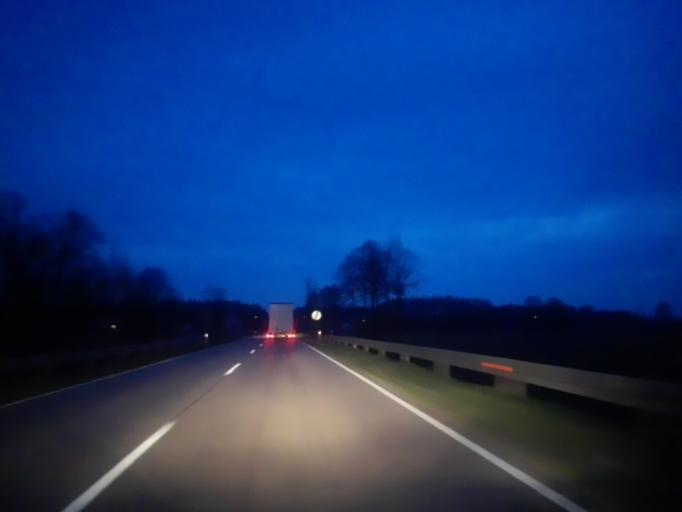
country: PL
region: Podlasie
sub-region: Powiat lomzynski
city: Sniadowo
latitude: 53.0331
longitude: 21.9764
